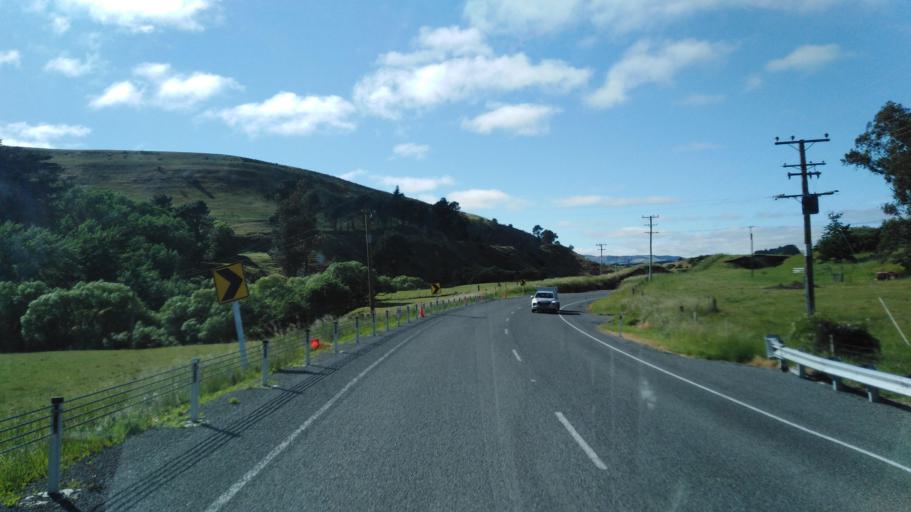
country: NZ
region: Canterbury
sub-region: Hurunui District
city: Amberley
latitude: -43.0187
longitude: 172.7081
